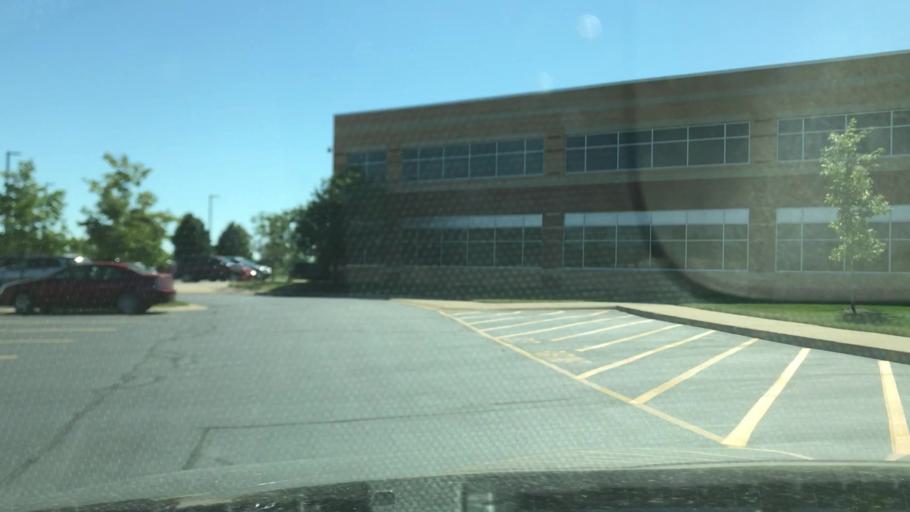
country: US
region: Michigan
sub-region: Ottawa County
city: Zeeland
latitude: 42.8208
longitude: -85.9873
